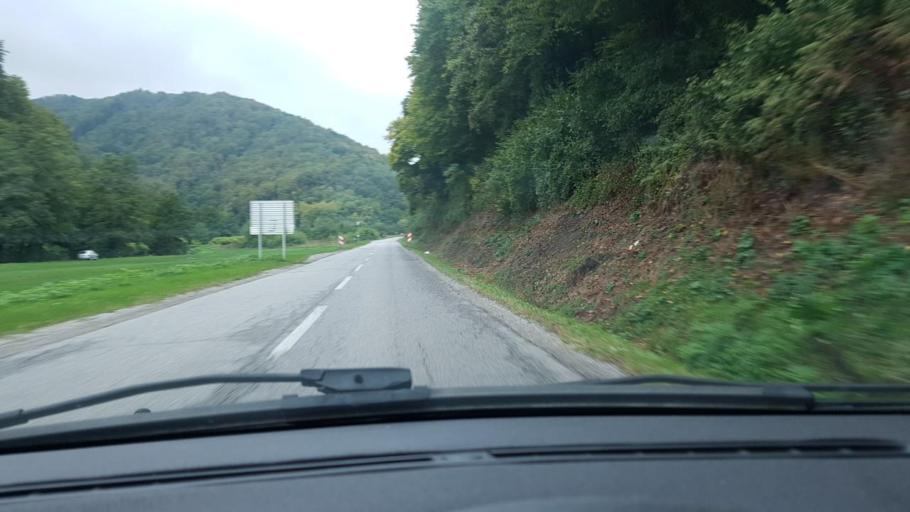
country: HR
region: Krapinsko-Zagorska
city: Marija Bistrica
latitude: 45.9314
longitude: 16.1153
